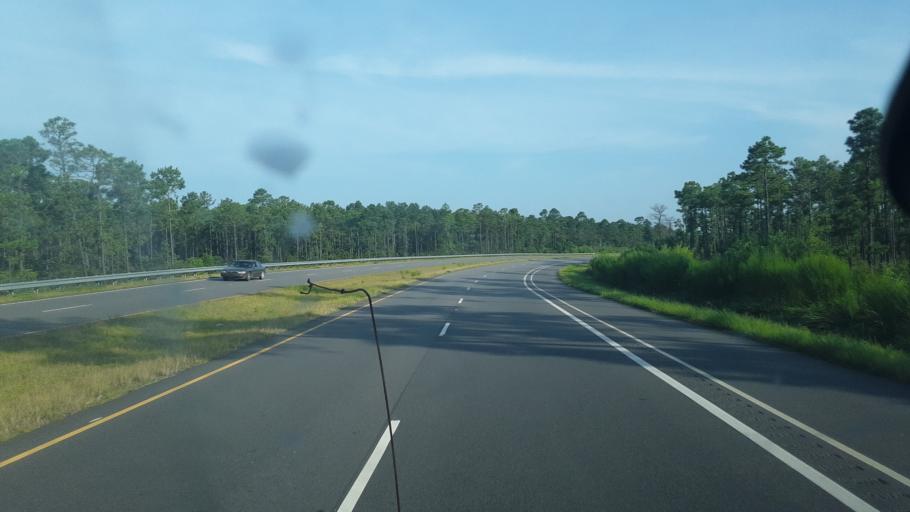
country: US
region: South Carolina
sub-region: Horry County
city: Myrtle Beach
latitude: 33.7923
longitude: -78.8818
